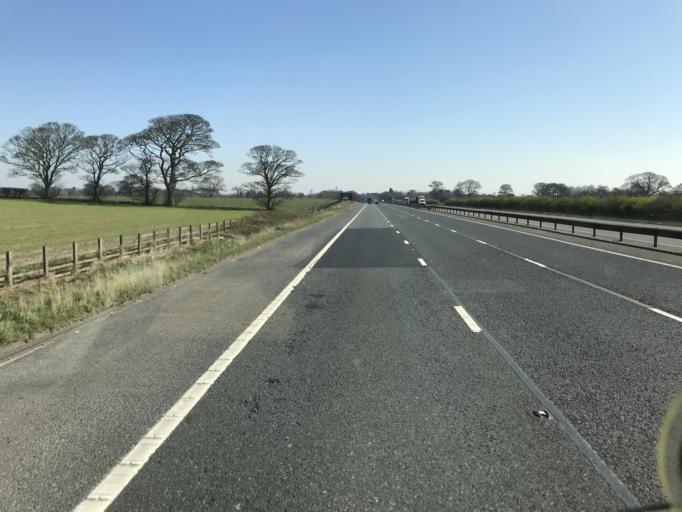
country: GB
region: England
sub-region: Warrington
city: Stretton
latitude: 53.3335
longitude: -2.5908
